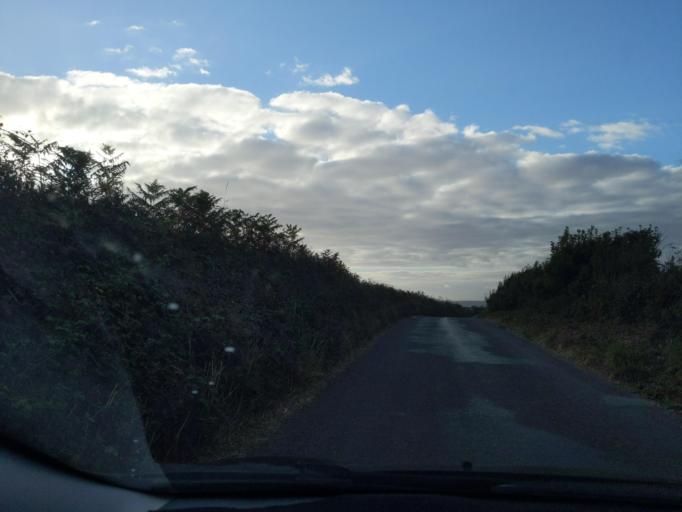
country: GB
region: England
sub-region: Devon
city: Salcombe
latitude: 50.2323
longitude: -3.8157
